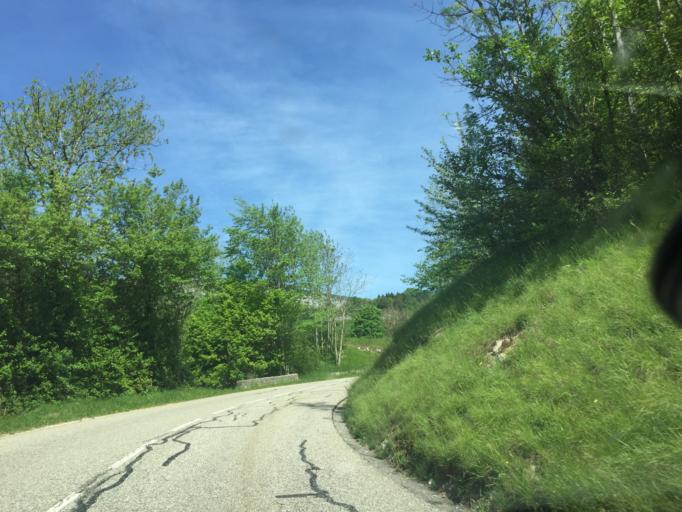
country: FR
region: Rhone-Alpes
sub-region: Departement de l'Isere
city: Barraux
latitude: 45.4443
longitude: 5.8805
